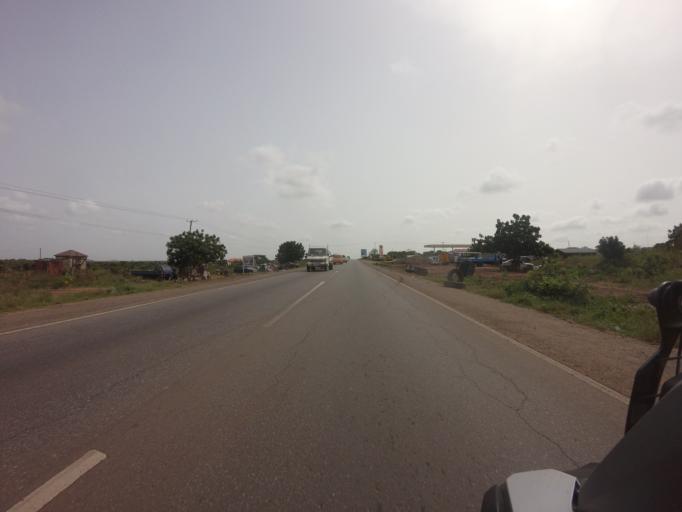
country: GH
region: Greater Accra
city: Tema
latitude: 5.7701
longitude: 0.0693
